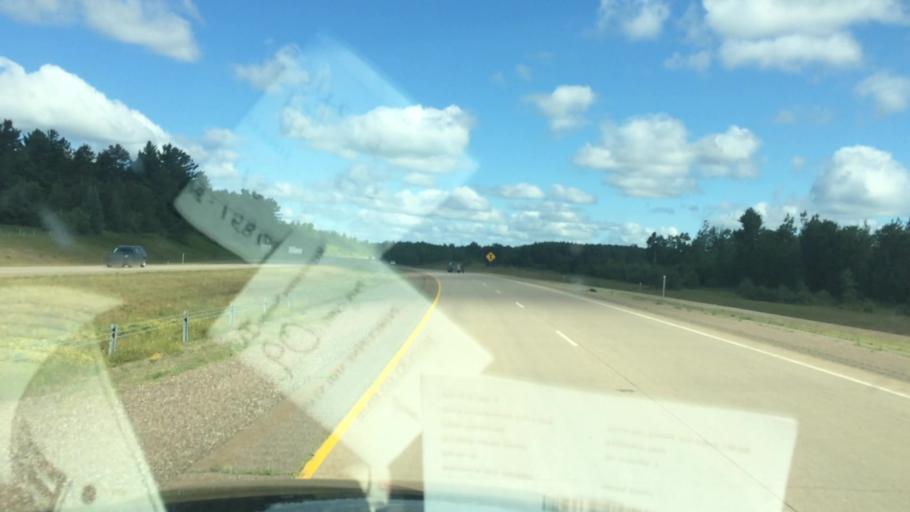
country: US
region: Wisconsin
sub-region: Lincoln County
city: Tomahawk
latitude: 45.4194
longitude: -89.6718
